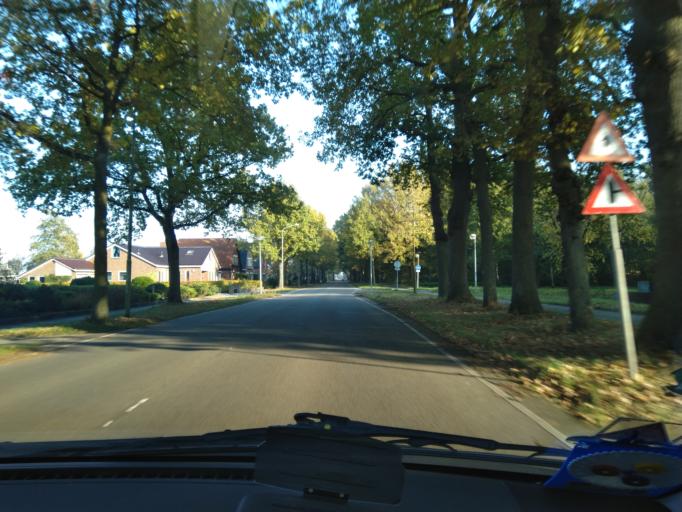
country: NL
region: Groningen
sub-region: Gemeente Hoogezand-Sappemeer
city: Sappemeer
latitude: 53.1547
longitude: 6.7888
